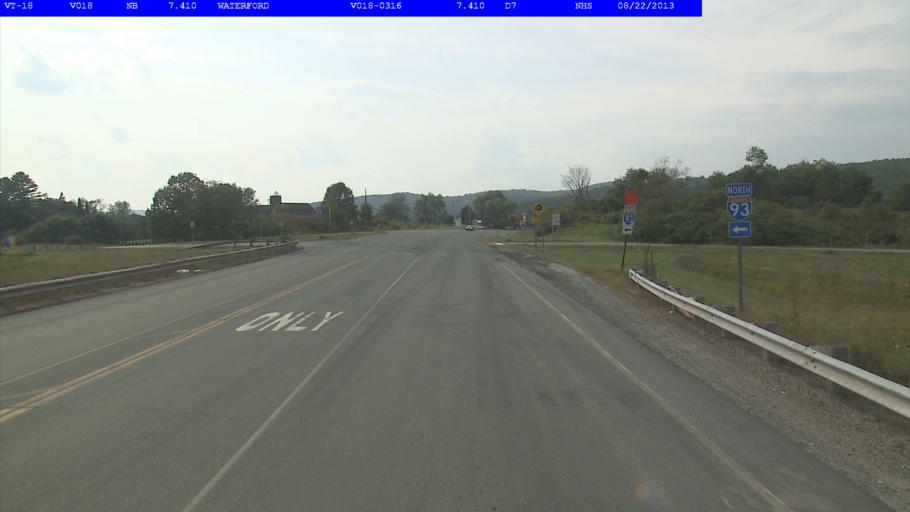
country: US
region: Vermont
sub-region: Caledonia County
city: St Johnsbury
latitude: 44.4259
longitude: -71.9556
